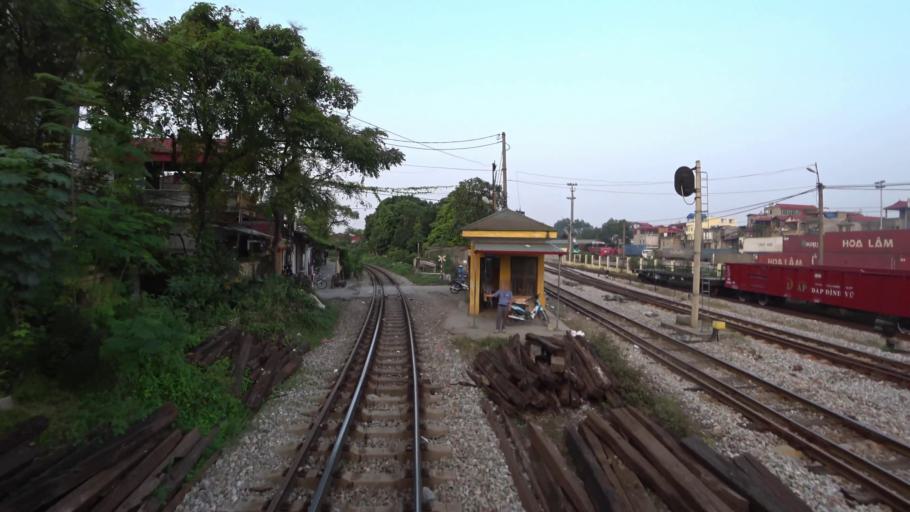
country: VN
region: Ha Noi
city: Dong Anh
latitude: 21.1073
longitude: 105.8996
